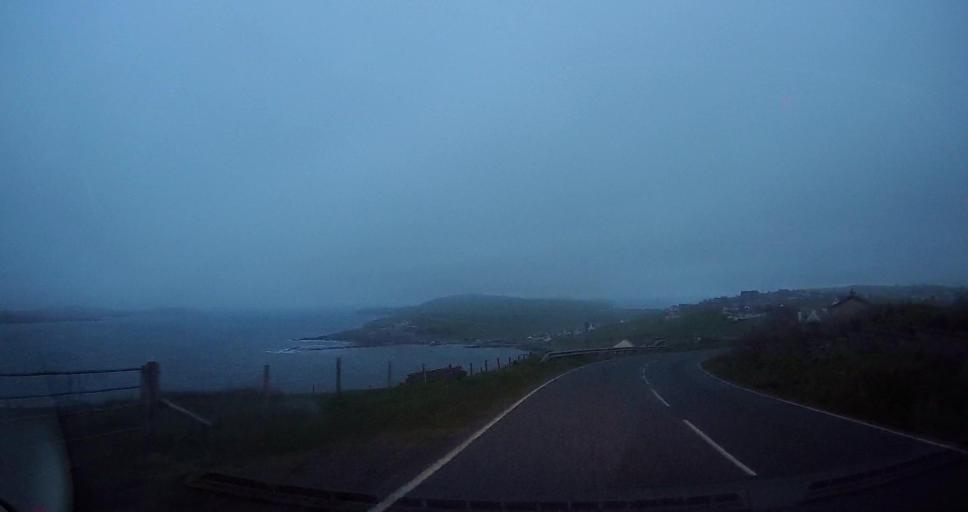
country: GB
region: Scotland
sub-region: Shetland Islands
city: Sandwick
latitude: 60.0134
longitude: -1.2265
